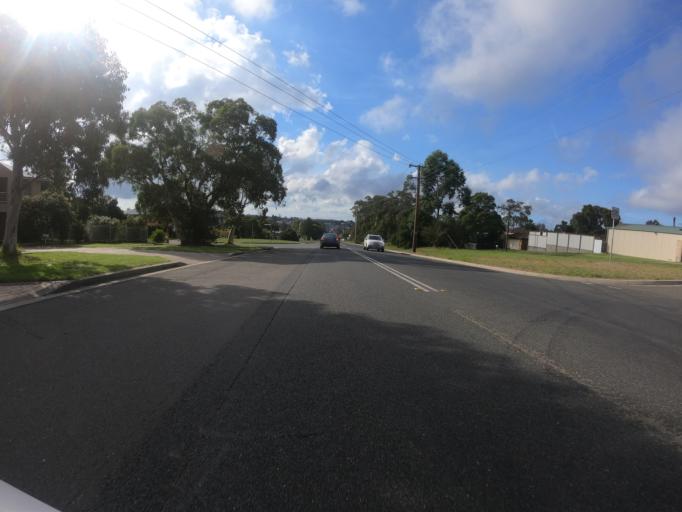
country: AU
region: New South Wales
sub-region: Wollongong
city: Helensburgh
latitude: -34.1996
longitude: 150.9803
